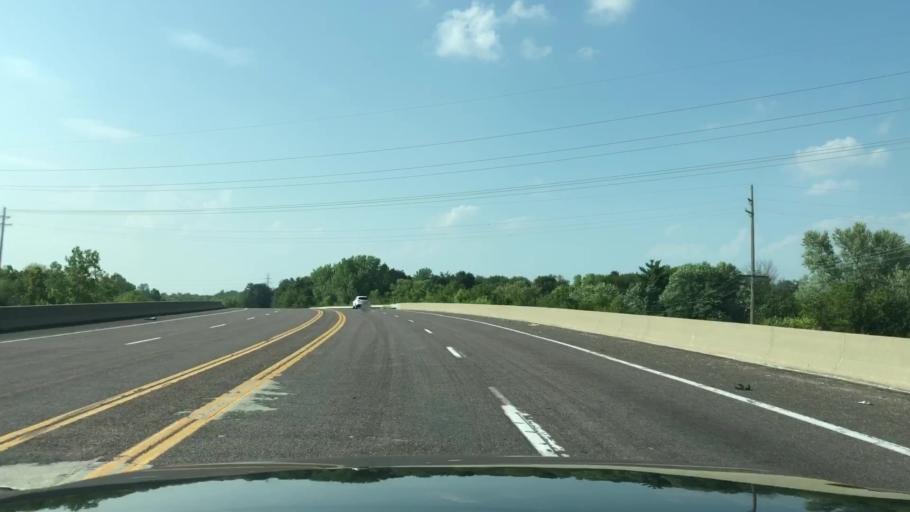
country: US
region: Missouri
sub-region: Saint Charles County
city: Lake Saint Louis
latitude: 38.8089
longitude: -90.8077
